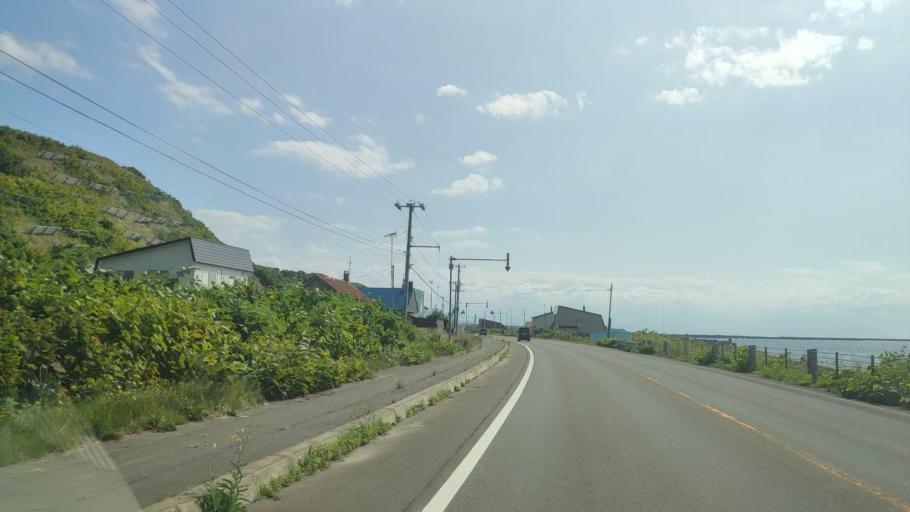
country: JP
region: Hokkaido
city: Rumoi
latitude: 43.9857
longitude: 141.6487
